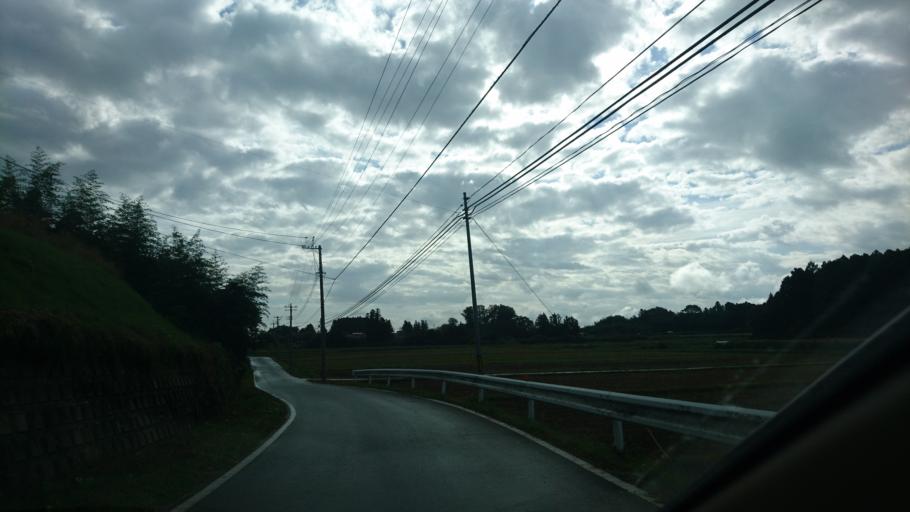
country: JP
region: Iwate
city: Ichinoseki
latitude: 38.7866
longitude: 141.0052
